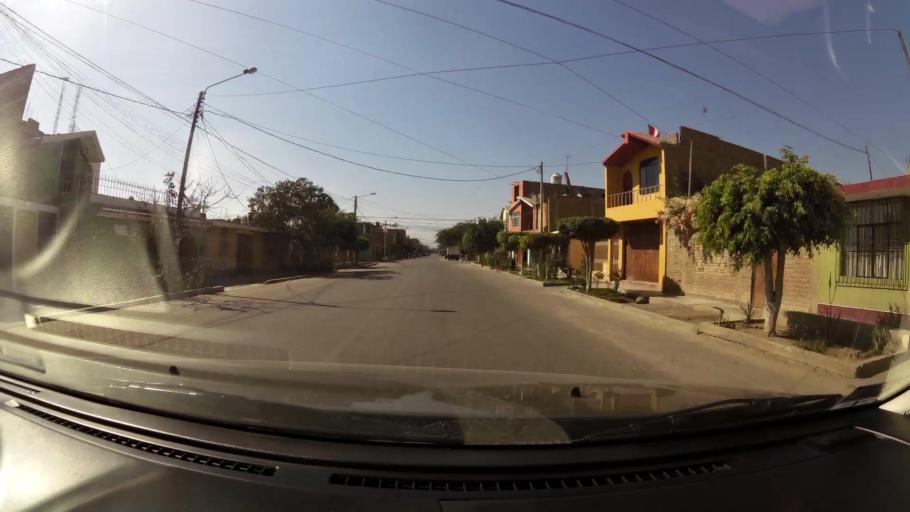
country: PE
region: Ica
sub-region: Provincia de Ica
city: La Tinguina
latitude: -14.0382
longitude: -75.7090
